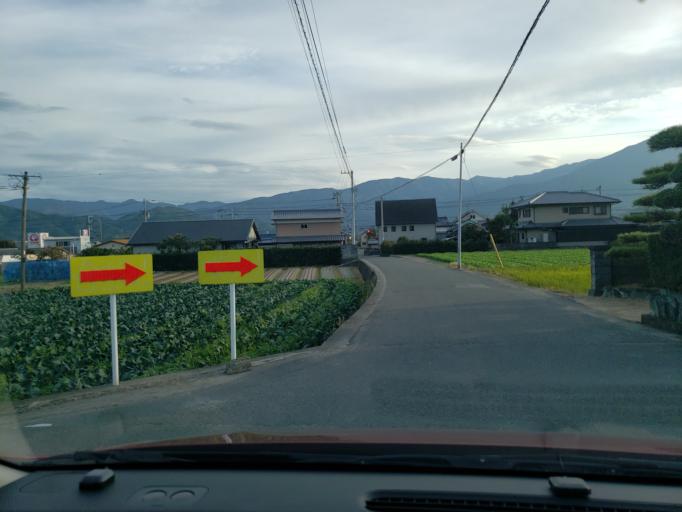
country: JP
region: Tokushima
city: Wakimachi
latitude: 34.0757
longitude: 134.2277
